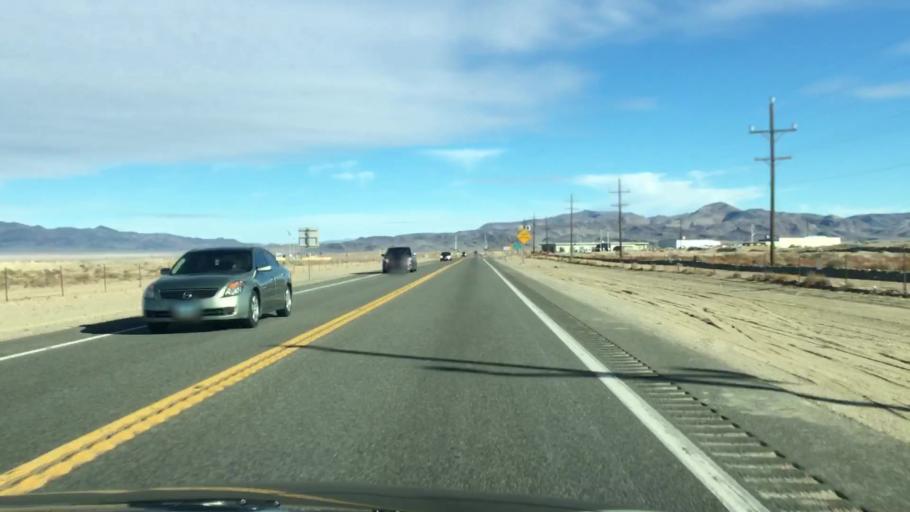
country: US
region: Nevada
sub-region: Mineral County
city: Hawthorne
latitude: 38.5245
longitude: -118.6023
